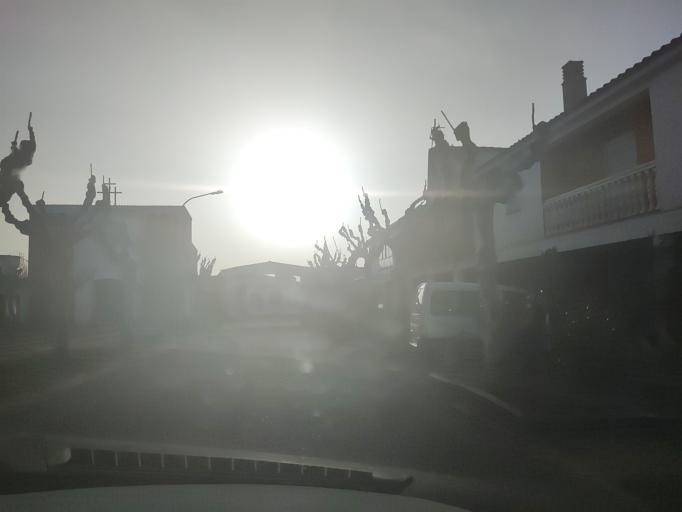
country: ES
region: Castille and Leon
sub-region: Provincia de Salamanca
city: Ciudad Rodrigo
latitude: 40.5707
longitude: -6.4915
